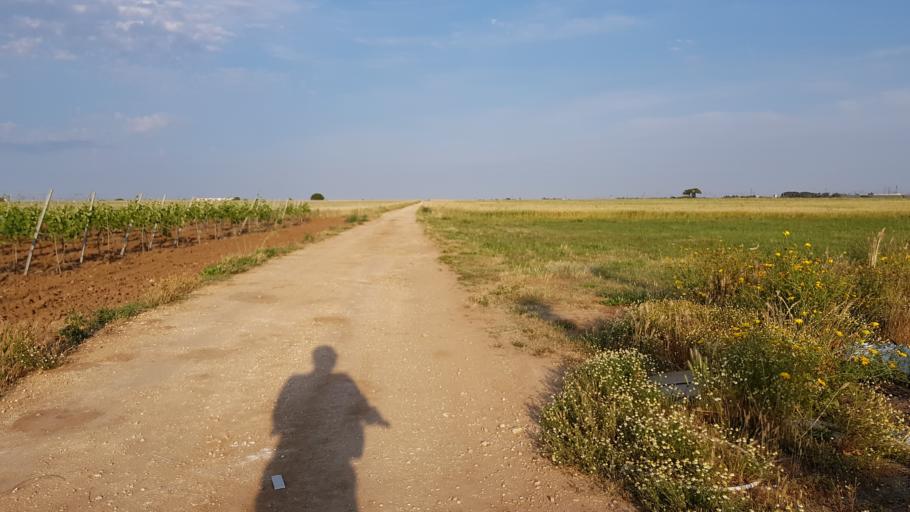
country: IT
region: Apulia
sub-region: Provincia di Brindisi
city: Brindisi
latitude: 40.6265
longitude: 17.8720
